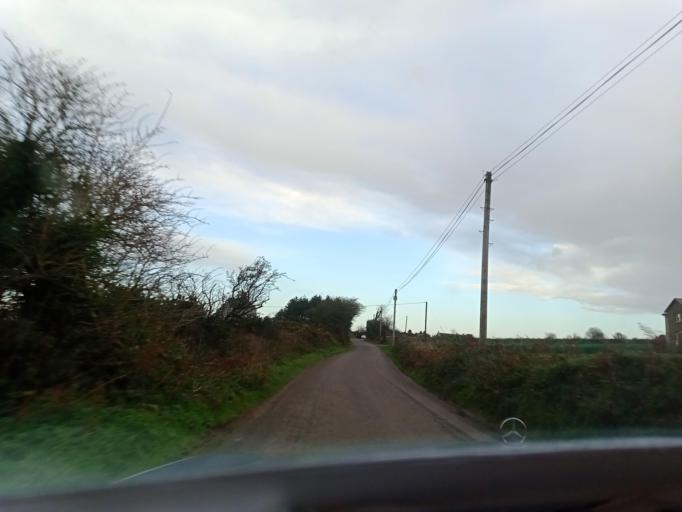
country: IE
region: Munster
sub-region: Waterford
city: Waterford
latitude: 52.3390
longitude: -7.0342
